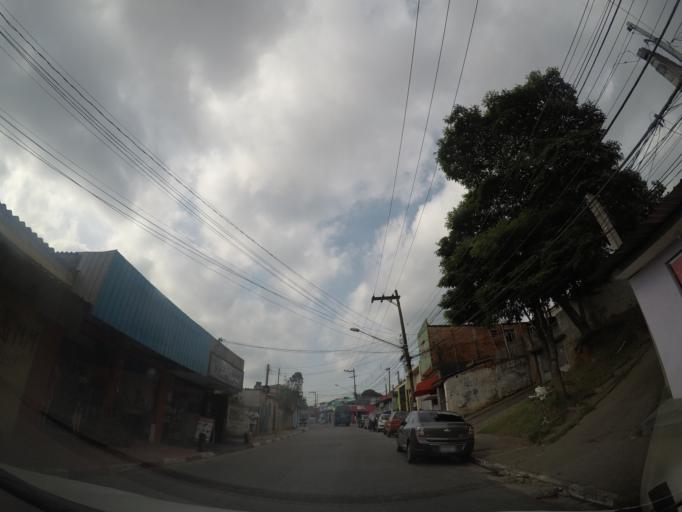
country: BR
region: Sao Paulo
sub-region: Guarulhos
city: Guarulhos
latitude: -23.4166
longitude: -46.5074
